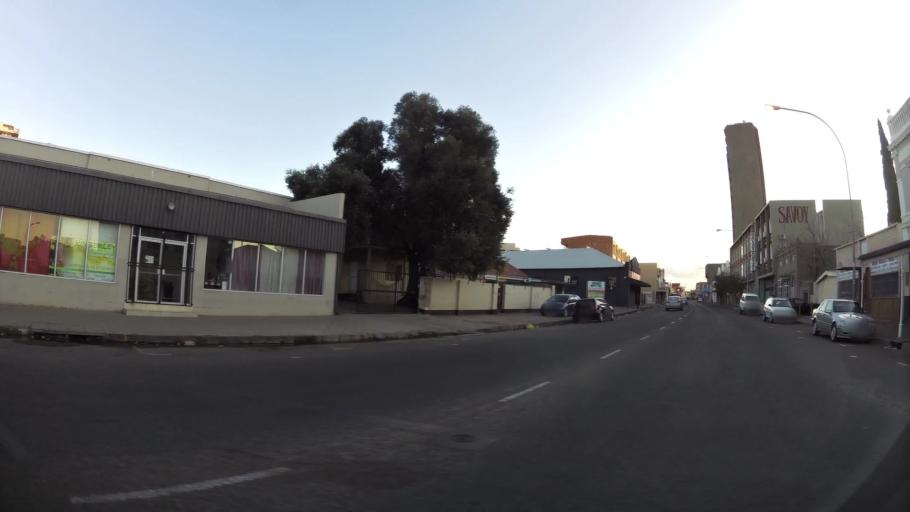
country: ZA
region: Northern Cape
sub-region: Frances Baard District Municipality
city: Kimberley
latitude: -28.7377
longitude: 24.7674
